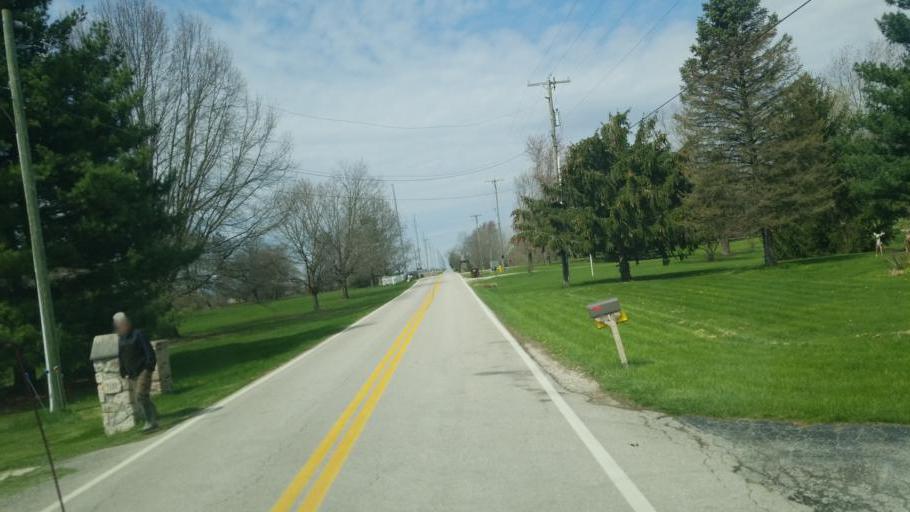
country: US
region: Ohio
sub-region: Delaware County
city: Delaware
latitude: 40.3647
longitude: -83.0803
